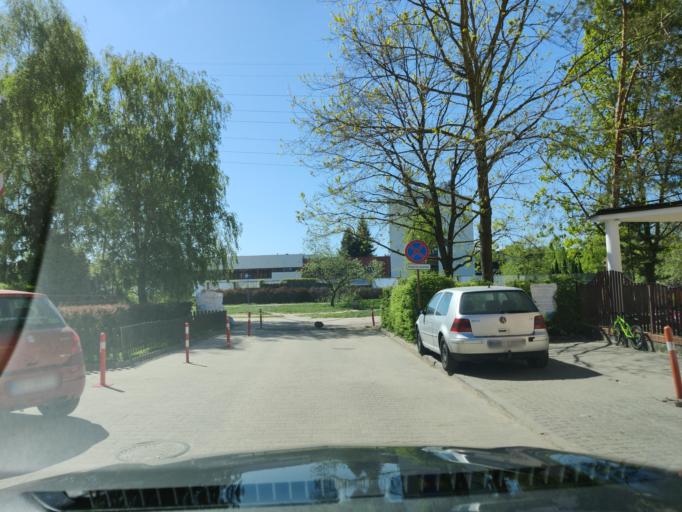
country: PL
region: Masovian Voivodeship
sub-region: Warszawa
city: Kabaty
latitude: 52.1277
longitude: 21.0635
